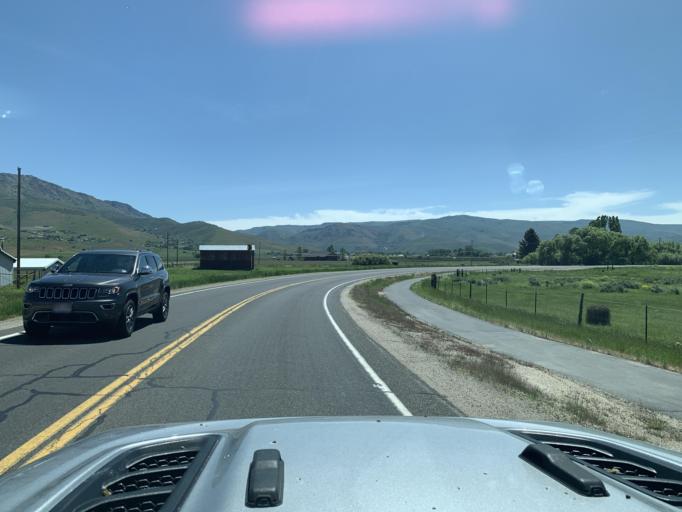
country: US
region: Utah
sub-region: Weber County
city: Wolf Creek
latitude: 41.2678
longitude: -111.7638
